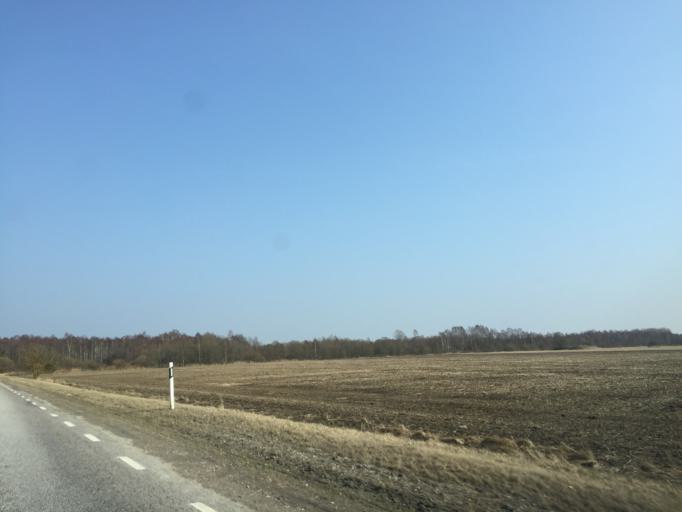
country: EE
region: Saare
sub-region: Kuressaare linn
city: Kuressaare
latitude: 58.4028
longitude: 22.7680
